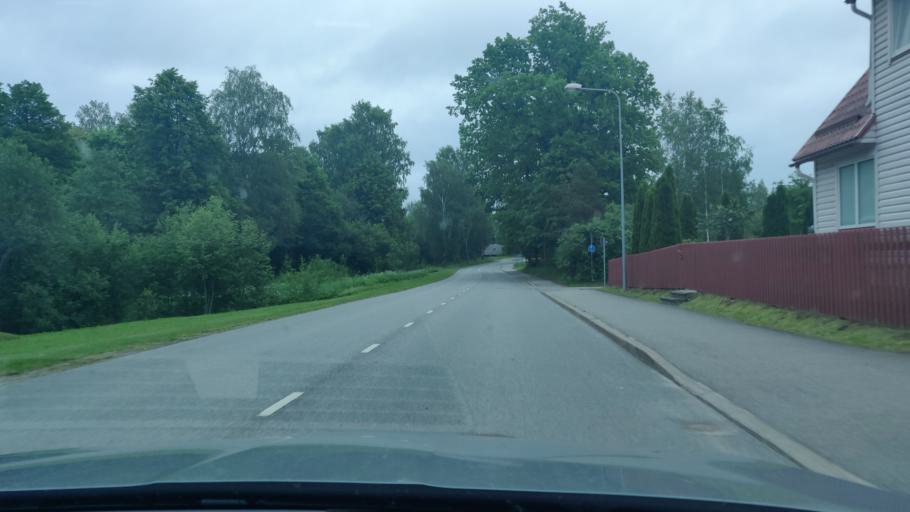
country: EE
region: Vorumaa
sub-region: Voru linn
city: Voru
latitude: 57.7306
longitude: 27.2872
